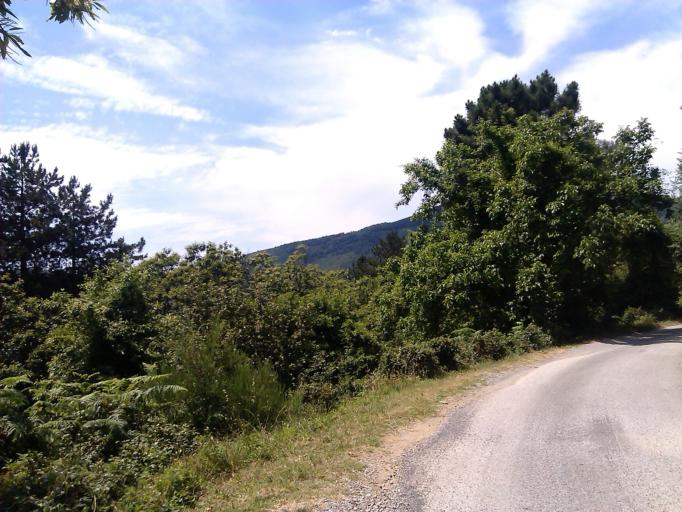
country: IT
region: Tuscany
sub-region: Provincia di Pistoia
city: Montale
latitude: 43.9745
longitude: 11.0383
